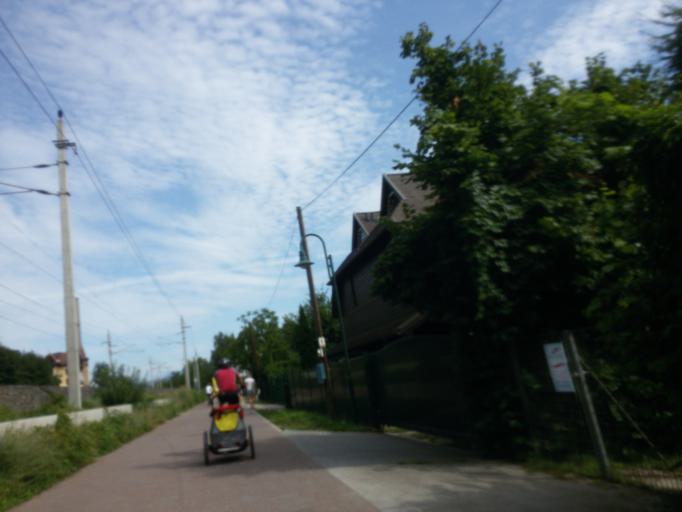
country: AT
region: Carinthia
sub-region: Klagenfurt am Woerthersee
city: Klagenfurt am Woerthersee
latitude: 46.6250
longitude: 14.2465
